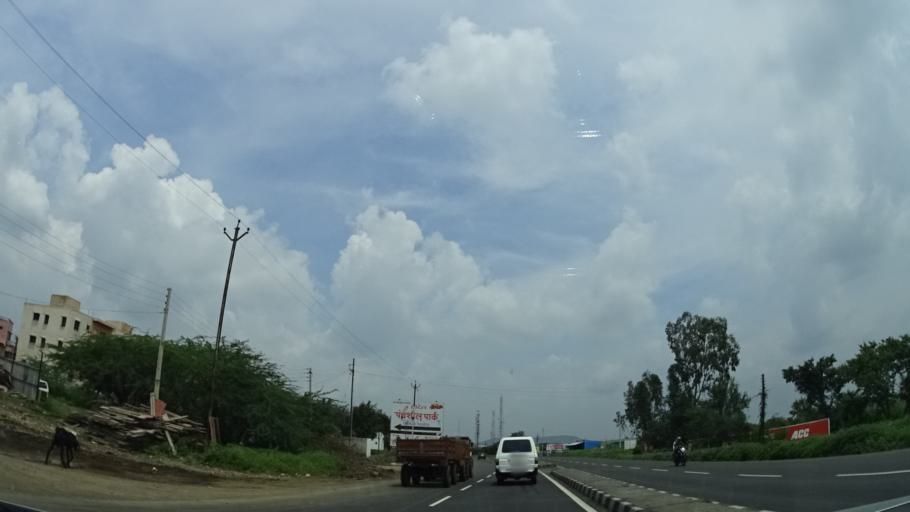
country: IN
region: Maharashtra
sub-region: Pune Division
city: Sirur
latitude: 18.9543
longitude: 74.5324
